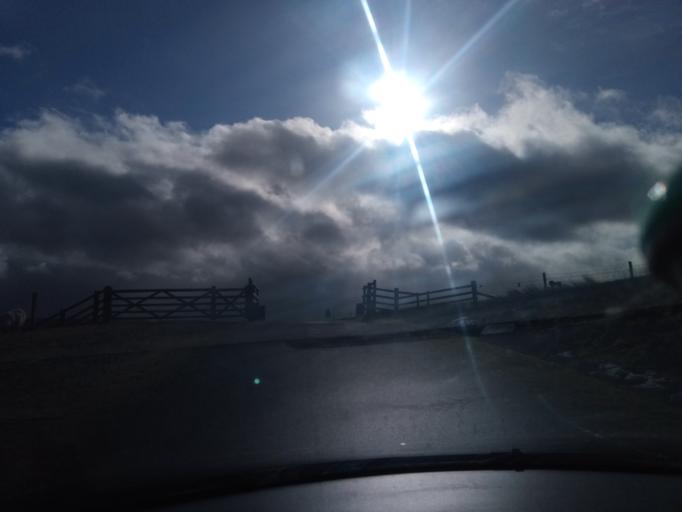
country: GB
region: England
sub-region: Northumberland
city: Rochester
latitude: 55.3262
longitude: -2.2923
